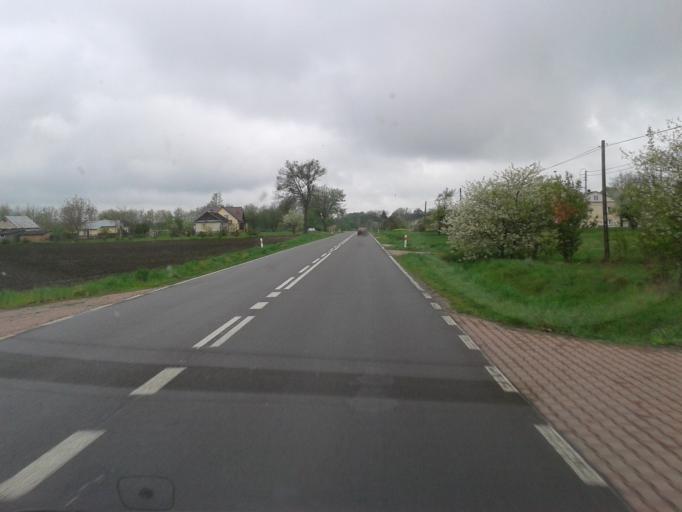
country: PL
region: Lublin Voivodeship
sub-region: Powiat hrubieszowski
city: Dolhobyczow
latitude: 50.5869
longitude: 24.0122
